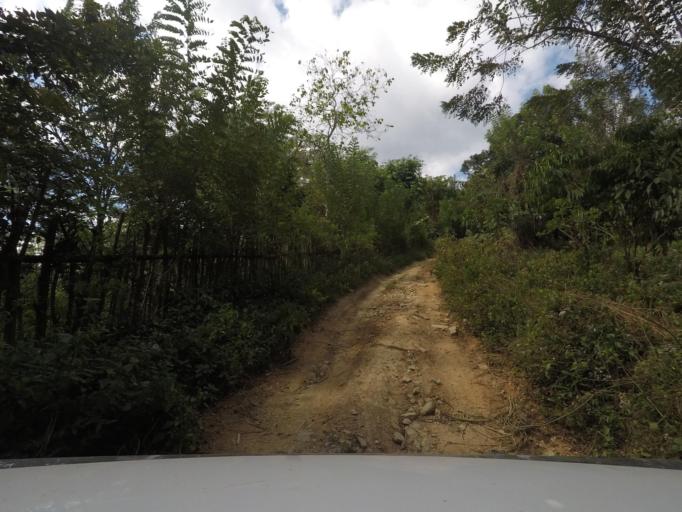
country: TL
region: Ermera
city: Gleno
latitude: -8.7183
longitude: 125.3116
